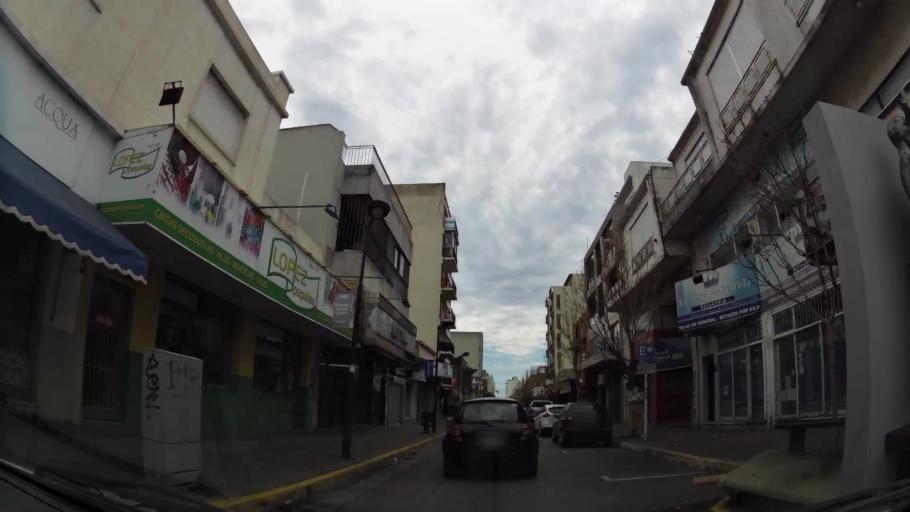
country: AR
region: Buenos Aires
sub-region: Partido de Quilmes
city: Quilmes
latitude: -34.7607
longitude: -58.2102
